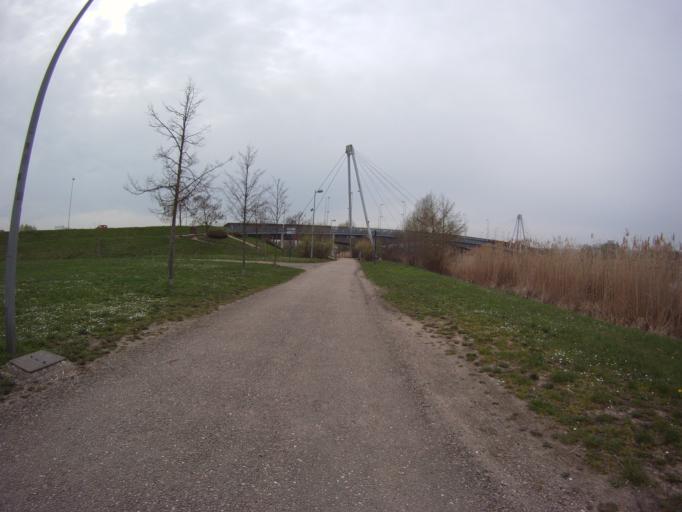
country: FR
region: Lorraine
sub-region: Departement de Meurthe-et-Moselle
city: Tomblaine
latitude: 48.6924
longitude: 6.2069
